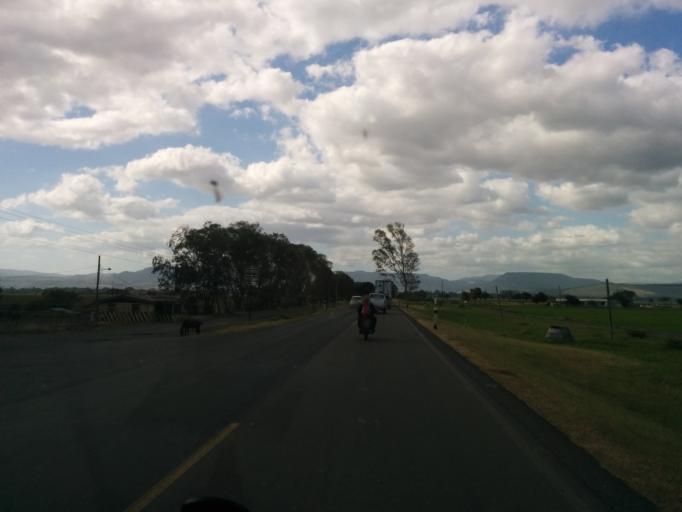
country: NI
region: Matagalpa
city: Ciudad Dario
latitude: 12.8663
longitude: -86.1166
